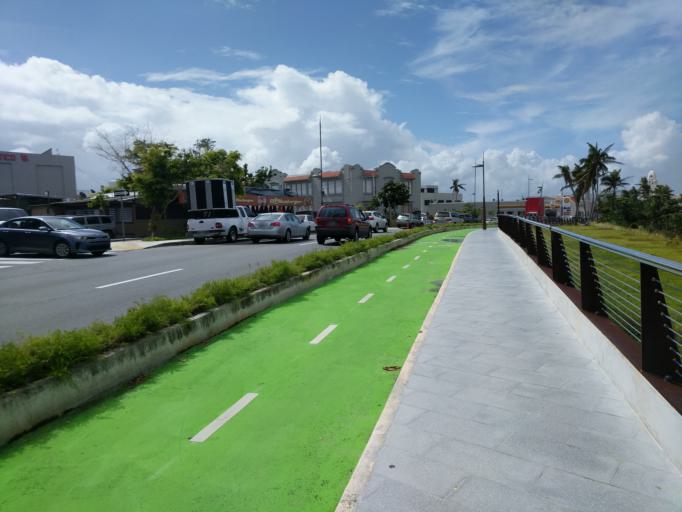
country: PR
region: San Juan
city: San Juan
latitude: 18.4659
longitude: -66.0948
